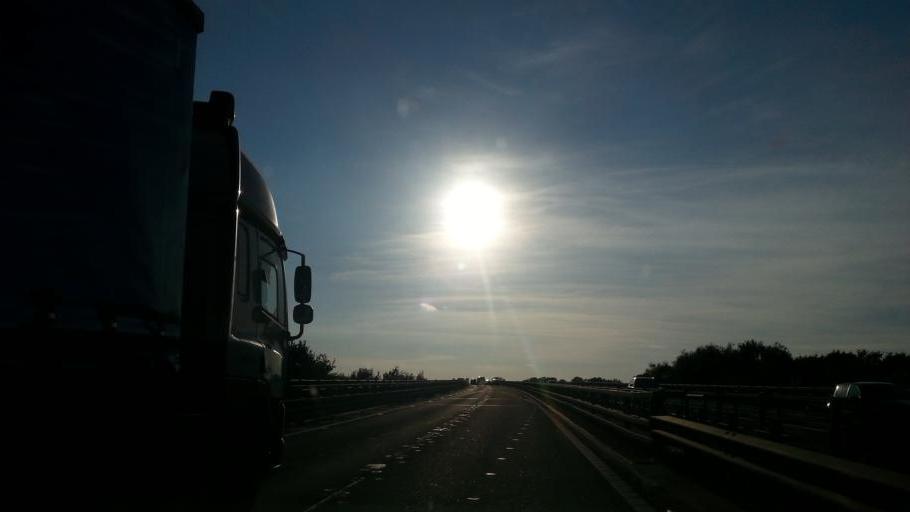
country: GB
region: England
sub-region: Worcestershire
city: Upton upon Severn
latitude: 52.0320
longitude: -2.1890
